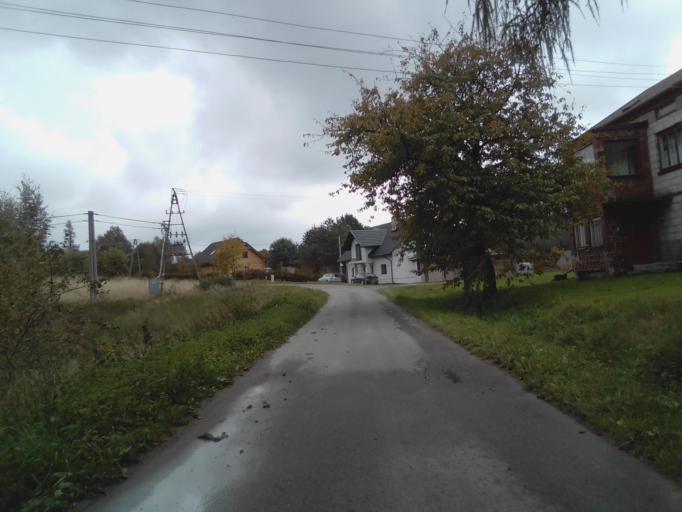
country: PL
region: Subcarpathian Voivodeship
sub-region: Powiat strzyzowski
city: Gwoznica Gorna
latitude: 49.8351
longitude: 22.0112
